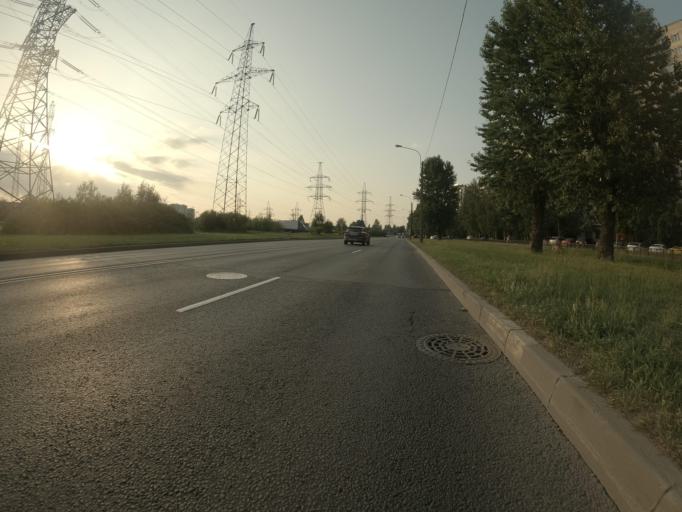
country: RU
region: St.-Petersburg
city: Krasnogvargeisky
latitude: 59.9515
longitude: 30.4608
